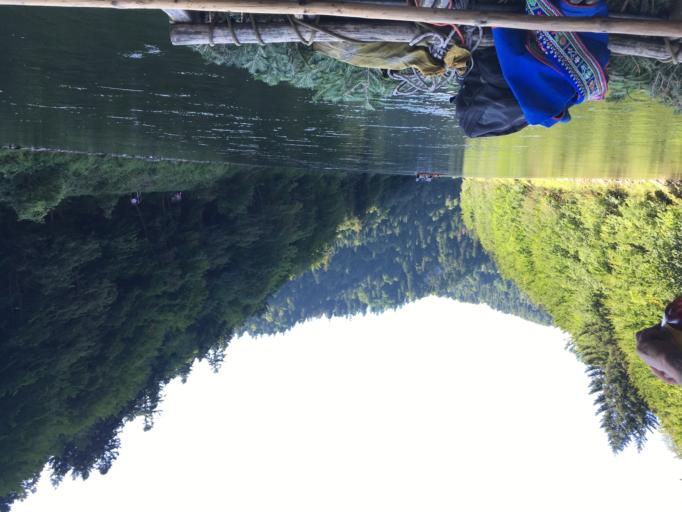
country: PL
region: Lesser Poland Voivodeship
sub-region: Powiat nowotarski
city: Kroscienko nad Dunajcem
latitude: 49.4005
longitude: 20.4287
